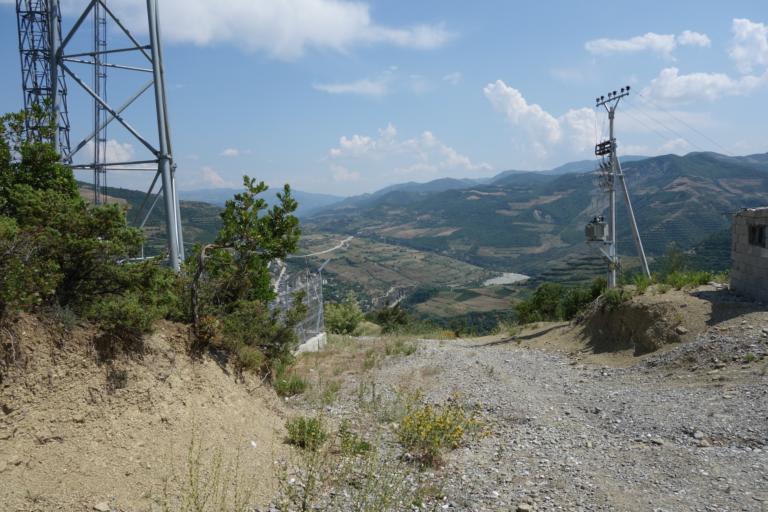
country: AL
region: Berat
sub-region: Rrethi i Skraparit
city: Corovode
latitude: 40.5124
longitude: 20.2188
